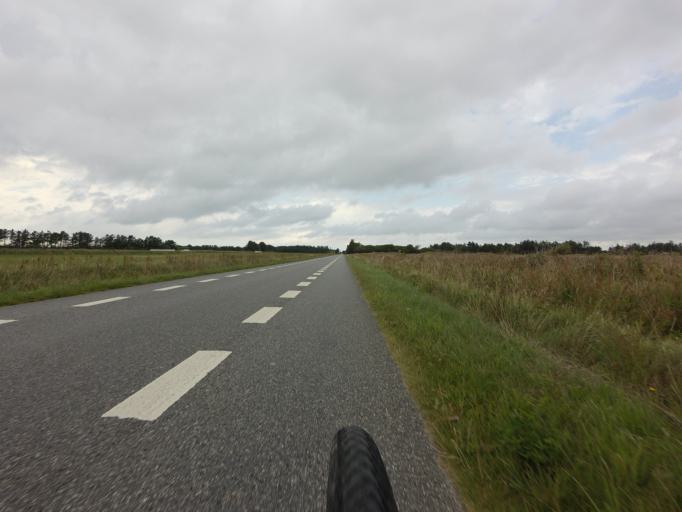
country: DK
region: North Denmark
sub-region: Hjorring Kommune
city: Hjorring
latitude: 57.4568
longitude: 9.7971
